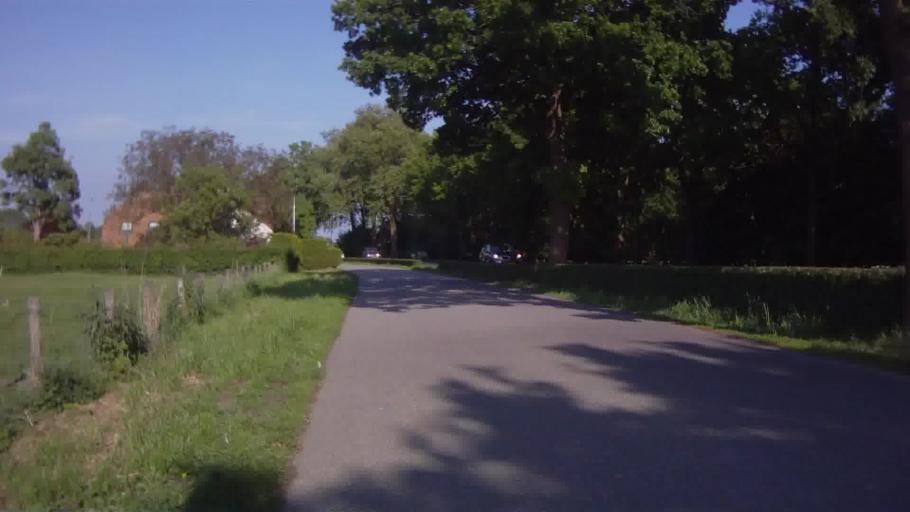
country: NL
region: Utrecht
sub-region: Gemeente Bunnik
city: Bunnik
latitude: 52.0641
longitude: 5.1832
